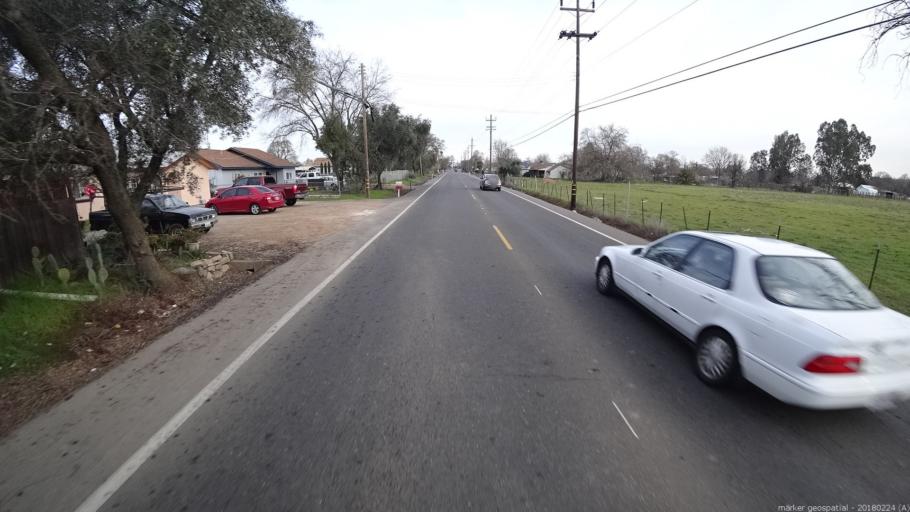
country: US
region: California
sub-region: Sacramento County
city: Rio Linda
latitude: 38.6789
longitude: -121.4570
